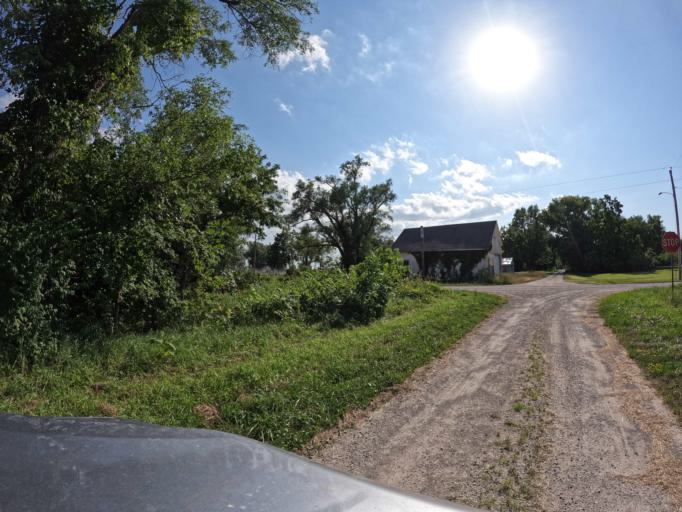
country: US
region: Iowa
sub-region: Appanoose County
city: Centerville
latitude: 40.7188
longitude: -93.0299
